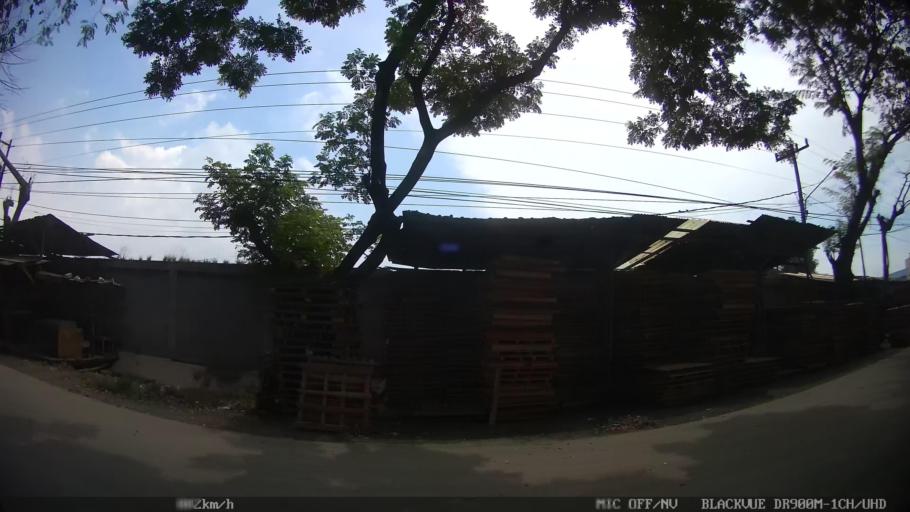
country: ID
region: North Sumatra
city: Labuhan Deli
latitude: 3.6712
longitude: 98.6776
